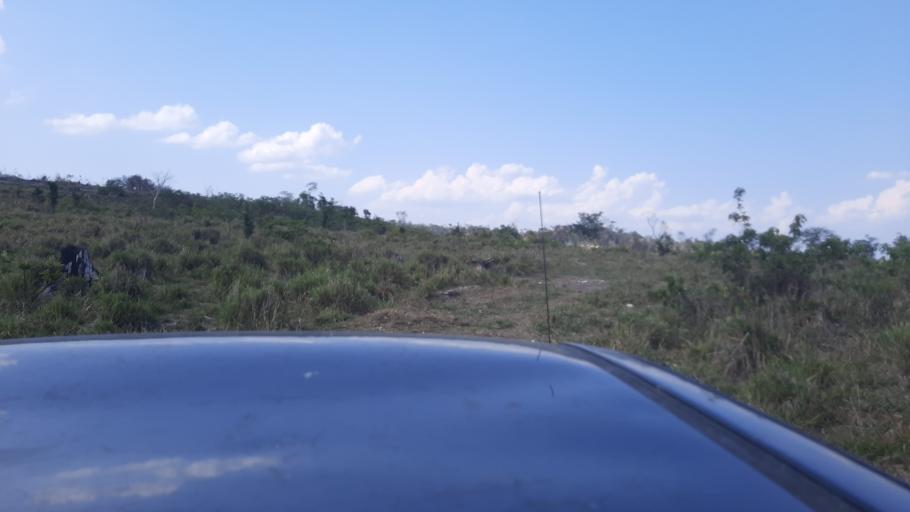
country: BZ
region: Cayo
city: Valley of Peace
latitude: 17.4028
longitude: -89.0395
